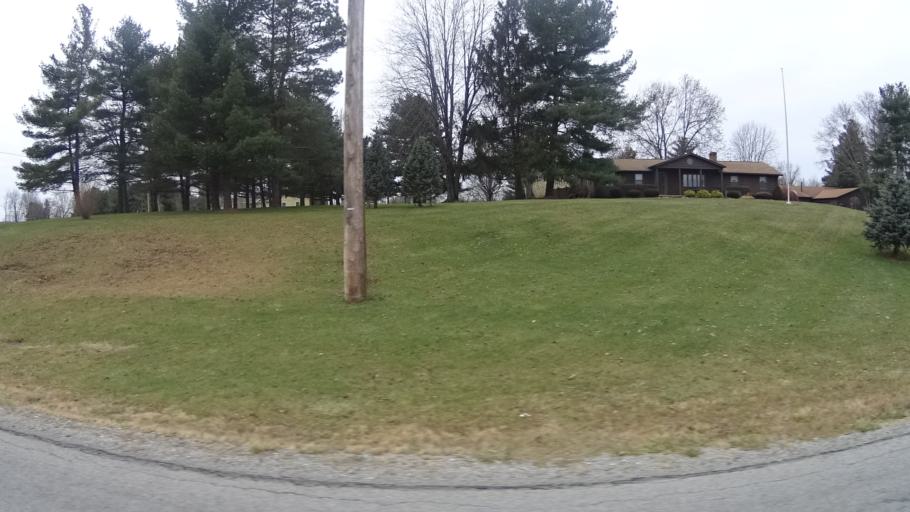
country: US
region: Ohio
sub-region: Lorain County
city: Wellington
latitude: 41.1706
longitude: -82.1934
